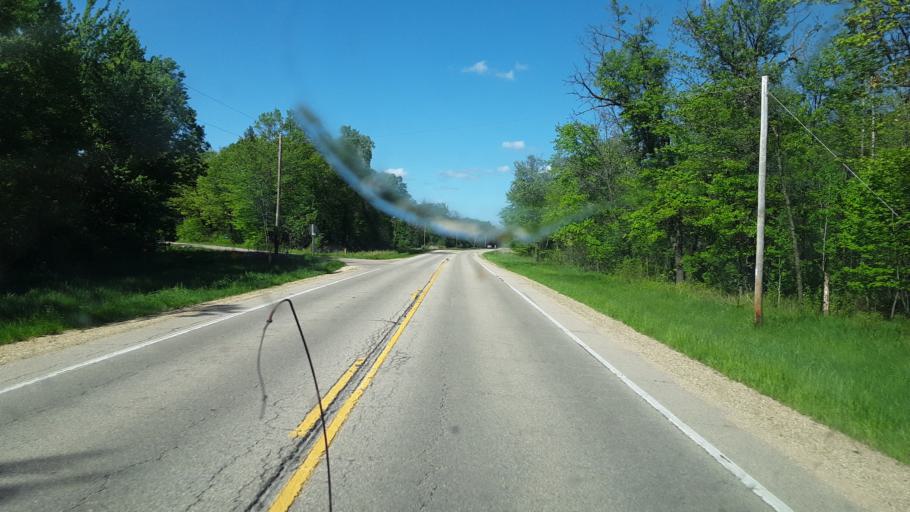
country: US
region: Wisconsin
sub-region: Juneau County
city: New Lisbon
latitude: 43.9146
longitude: -90.1226
